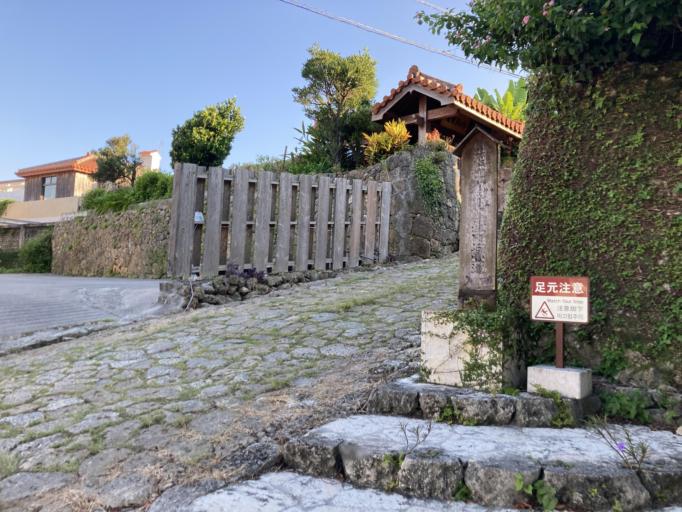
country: JP
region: Okinawa
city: Naha-shi
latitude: 26.2143
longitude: 127.7142
